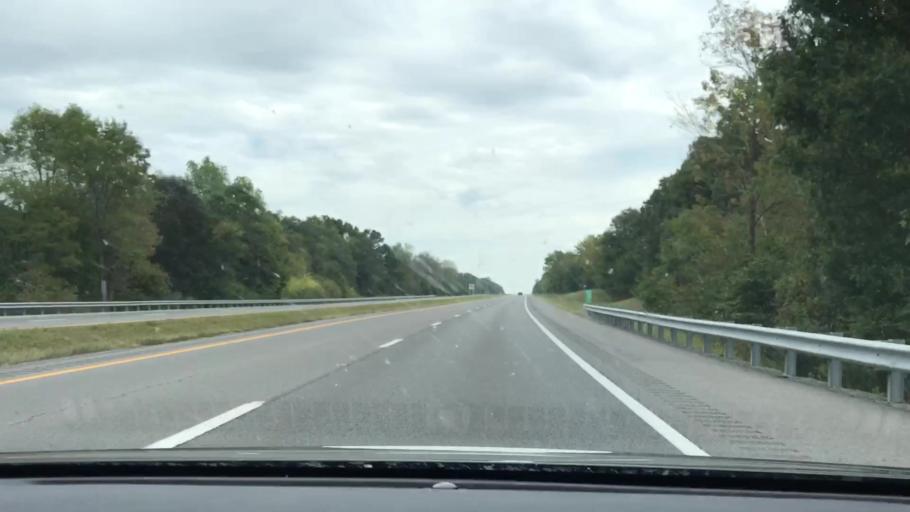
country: US
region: Kentucky
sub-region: Marshall County
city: Benton
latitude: 36.8208
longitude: -88.4782
